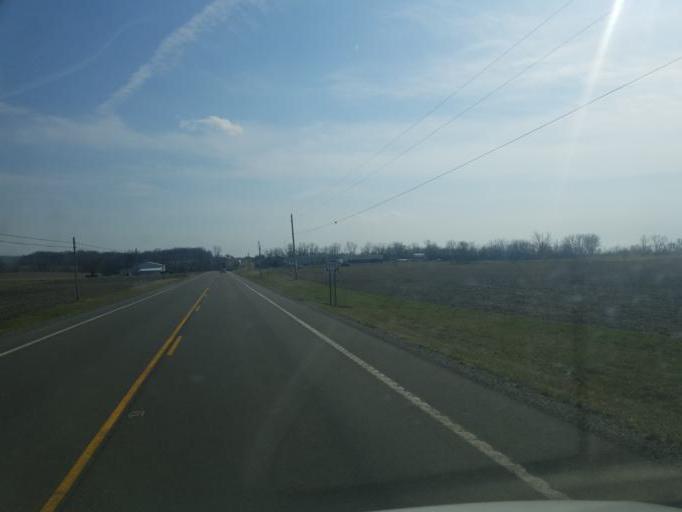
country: US
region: Ohio
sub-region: Logan County
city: Northwood
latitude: 40.5065
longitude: -83.6941
